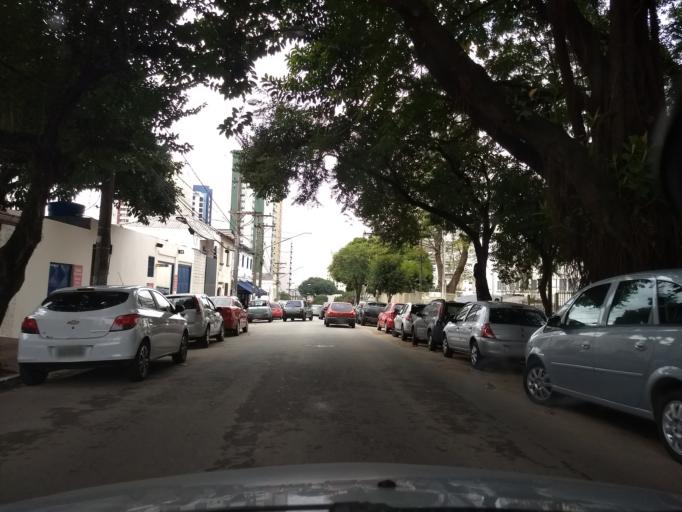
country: BR
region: Sao Paulo
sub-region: Sao Paulo
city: Sao Paulo
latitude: -23.5959
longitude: -46.6095
